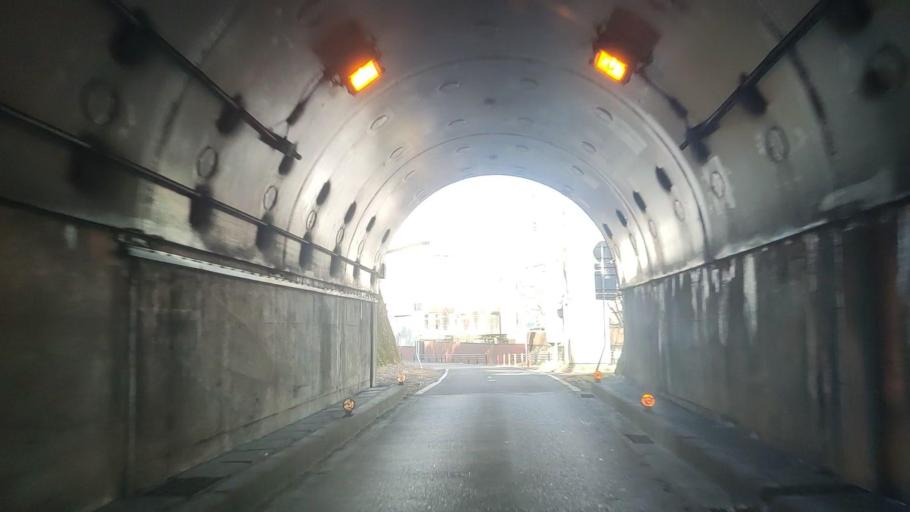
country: JP
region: Gifu
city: Gifu-shi
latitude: 35.4230
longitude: 136.7688
